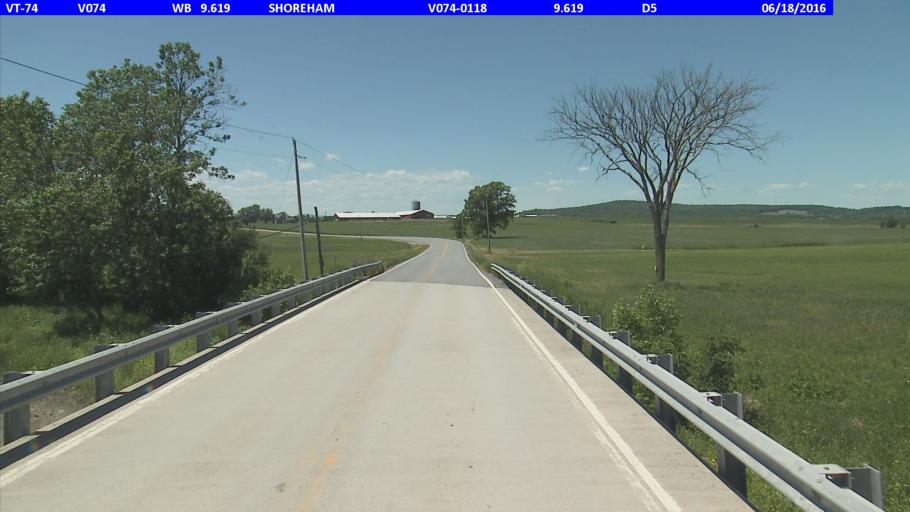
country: US
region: Vermont
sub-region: Addison County
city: Middlebury (village)
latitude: 43.9425
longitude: -73.2627
